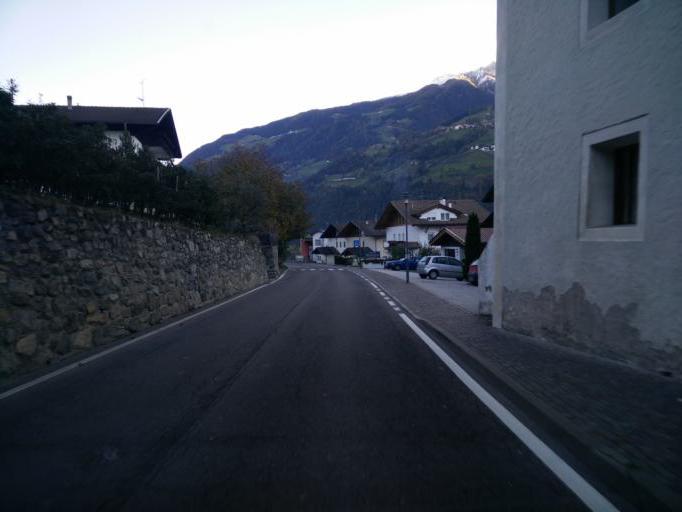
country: IT
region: Trentino-Alto Adige
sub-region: Bolzano
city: Rifiano
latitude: 46.7043
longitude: 11.1832
